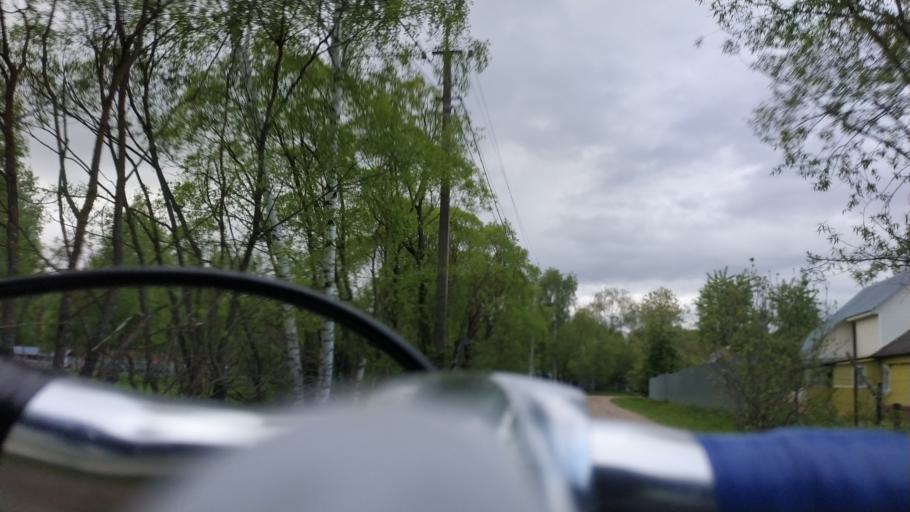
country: RU
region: Moskovskaya
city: Ramenskoye
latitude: 55.6096
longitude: 38.2828
